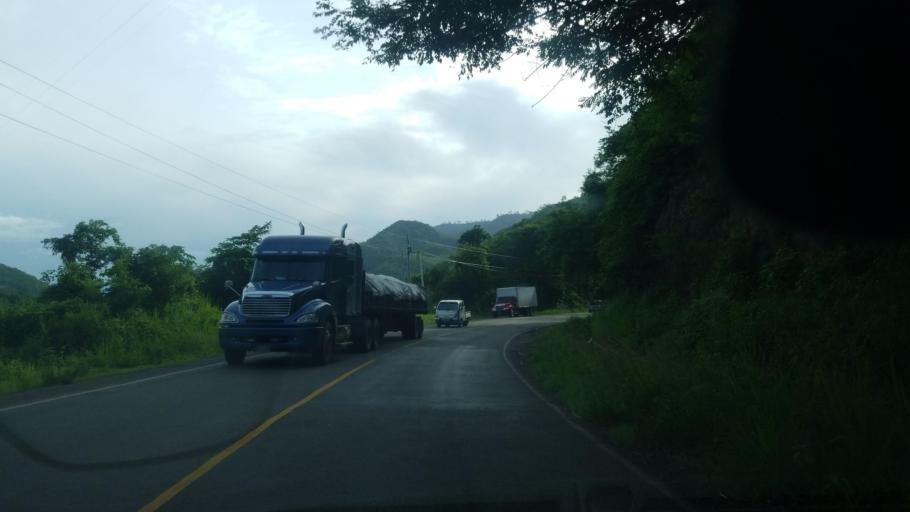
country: HN
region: Santa Barbara
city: Ilama
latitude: 15.0905
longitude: -88.2067
